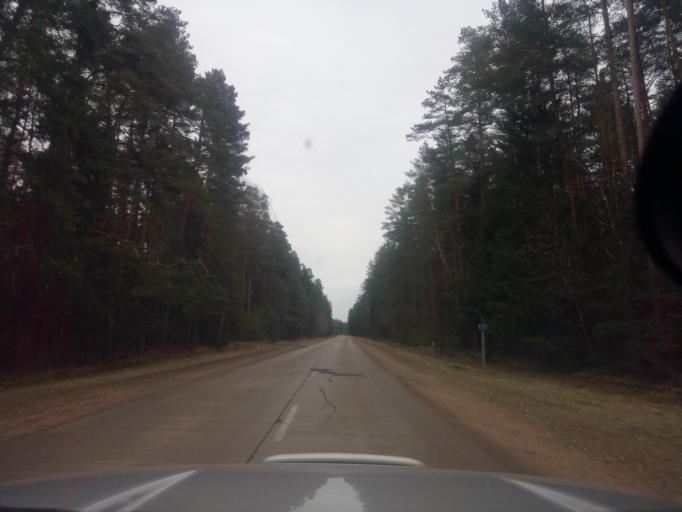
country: BY
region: Minsk
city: Uzda
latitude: 53.4625
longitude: 27.2583
